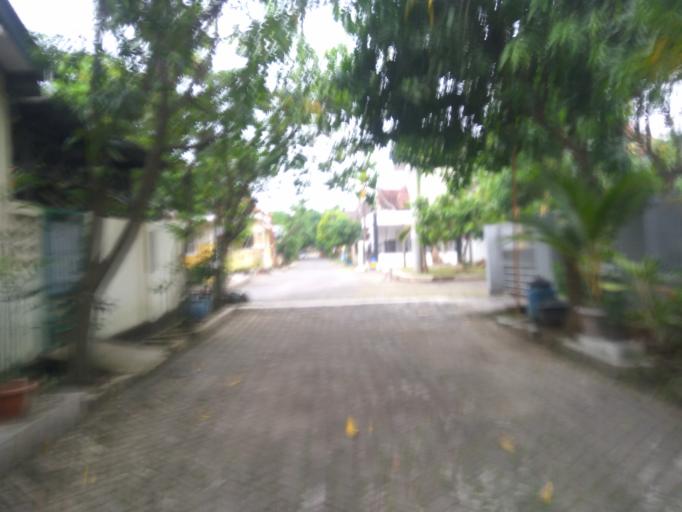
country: ID
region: Central Java
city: Mranggen
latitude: -7.0253
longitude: 110.4633
